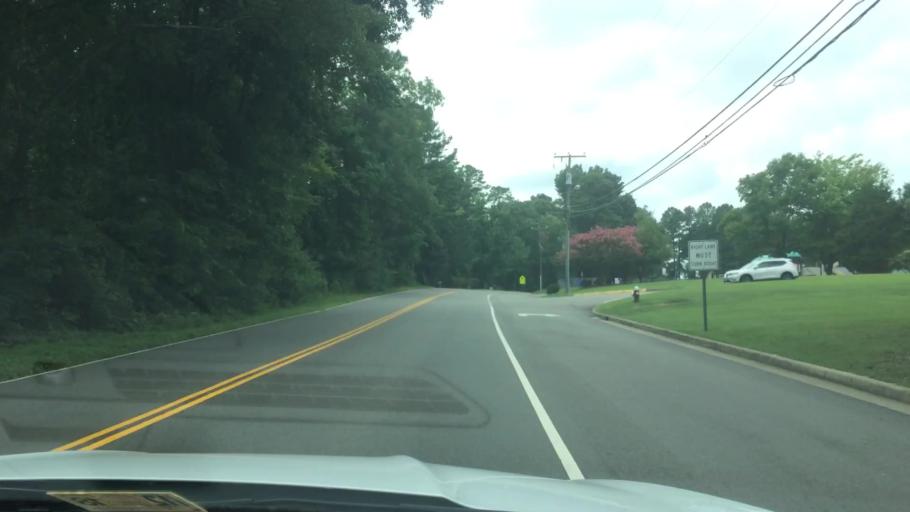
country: US
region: Virginia
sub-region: York County
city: Yorktown
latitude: 37.1622
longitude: -76.4565
